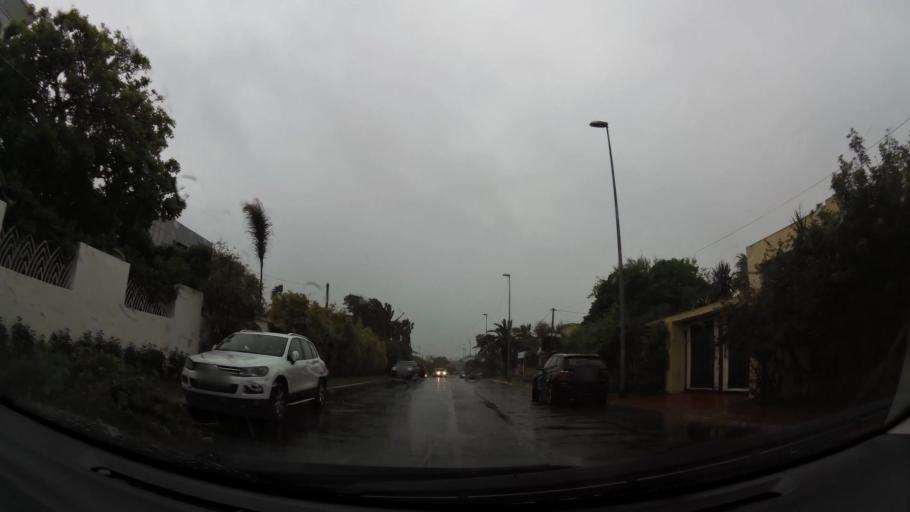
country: MA
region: Grand Casablanca
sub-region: Casablanca
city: Casablanca
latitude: 33.5936
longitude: -7.6698
